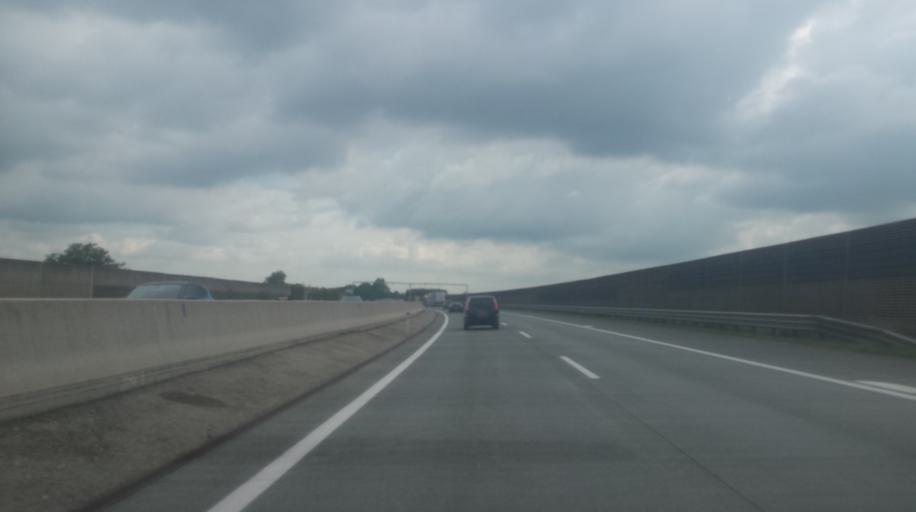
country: AT
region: Upper Austria
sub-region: Politischer Bezirk Vocklabruck
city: Desselbrunn
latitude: 47.9661
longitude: 13.7613
